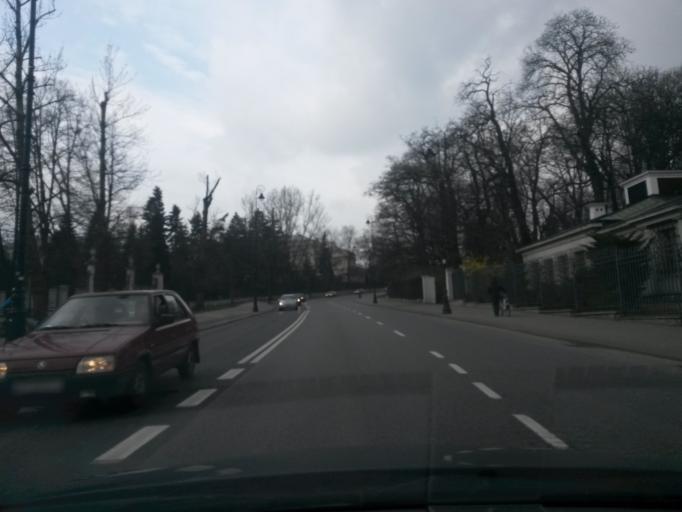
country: PL
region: Masovian Voivodeship
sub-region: Warszawa
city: Mokotow
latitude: 52.2109
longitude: 21.0275
